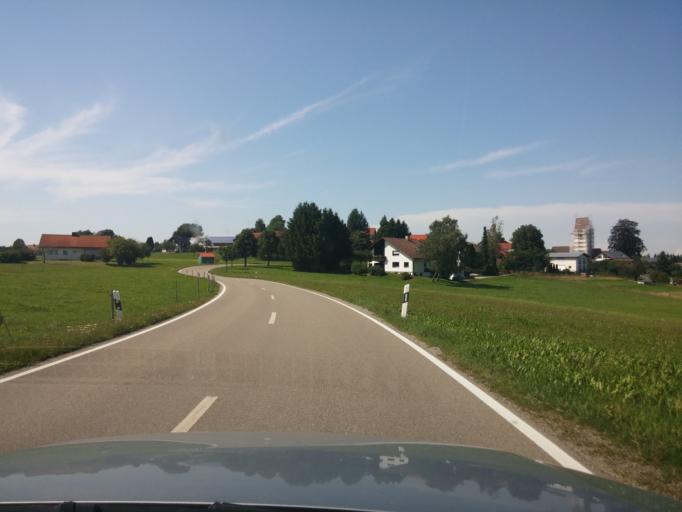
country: DE
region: Baden-Wuerttemberg
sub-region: Tuebingen Region
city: Aichstetten
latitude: 47.8579
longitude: 10.0702
